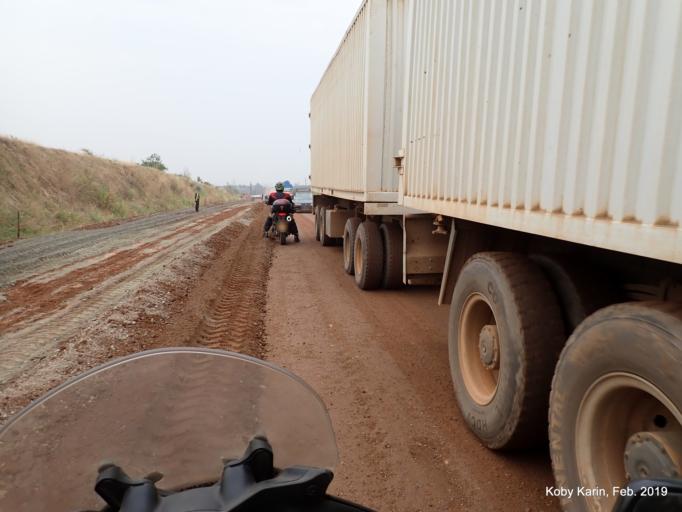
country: UG
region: Western Region
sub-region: Kasese District
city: Kasese
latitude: 0.3202
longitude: 30.1846
